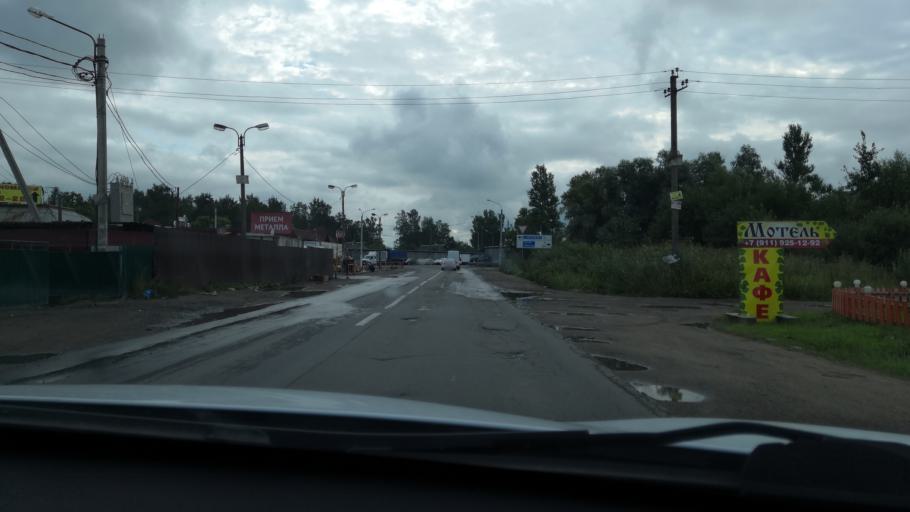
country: RU
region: St.-Petersburg
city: Kolpino
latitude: 59.7042
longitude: 30.5762
